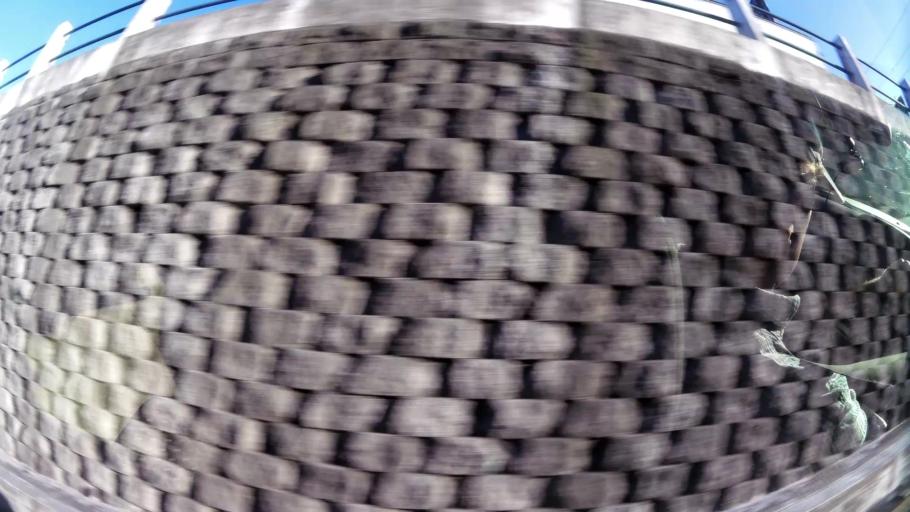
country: GT
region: Guatemala
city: Mixco
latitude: 14.6169
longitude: -90.6074
